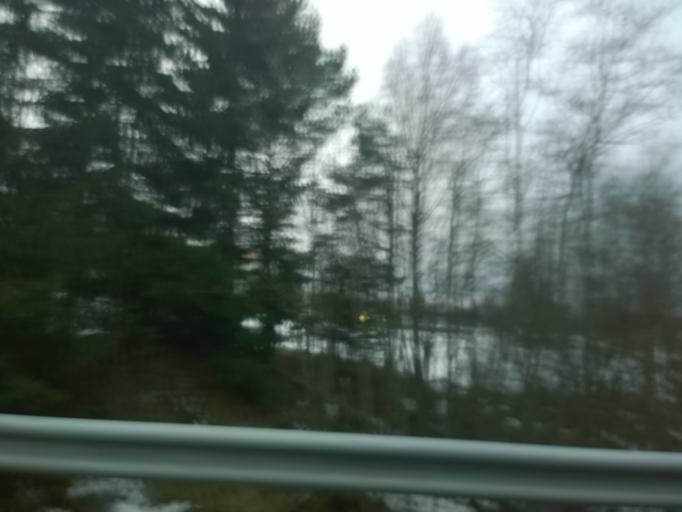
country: FI
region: Pirkanmaa
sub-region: Tampere
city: Lempaeaelae
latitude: 61.3780
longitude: 23.7795
